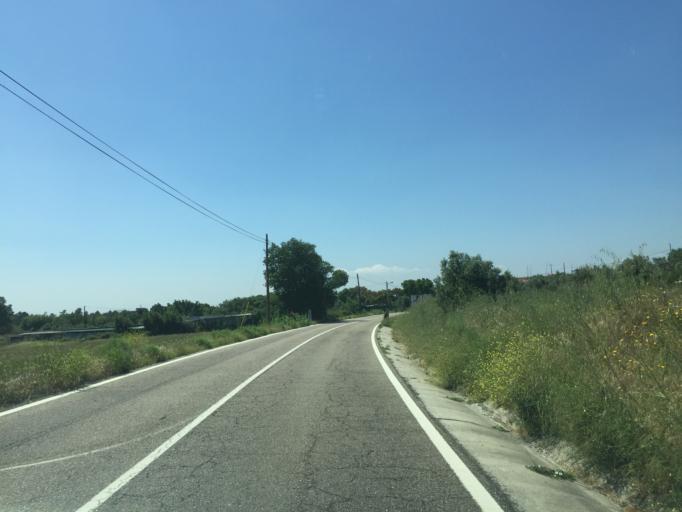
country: PT
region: Santarem
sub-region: Constancia
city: Constancia
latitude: 39.4809
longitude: -8.2980
